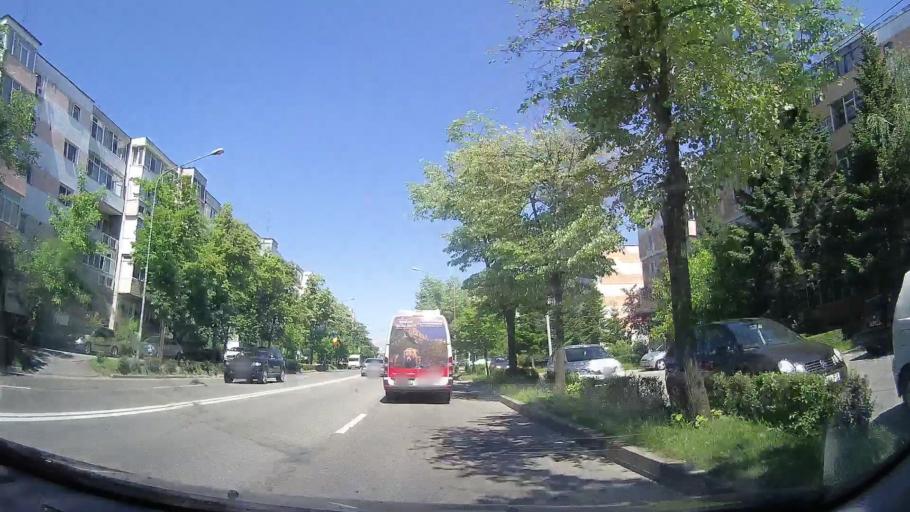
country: RO
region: Arges
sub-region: Comuna Bradu
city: Geamana
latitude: 44.8326
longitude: 24.9075
